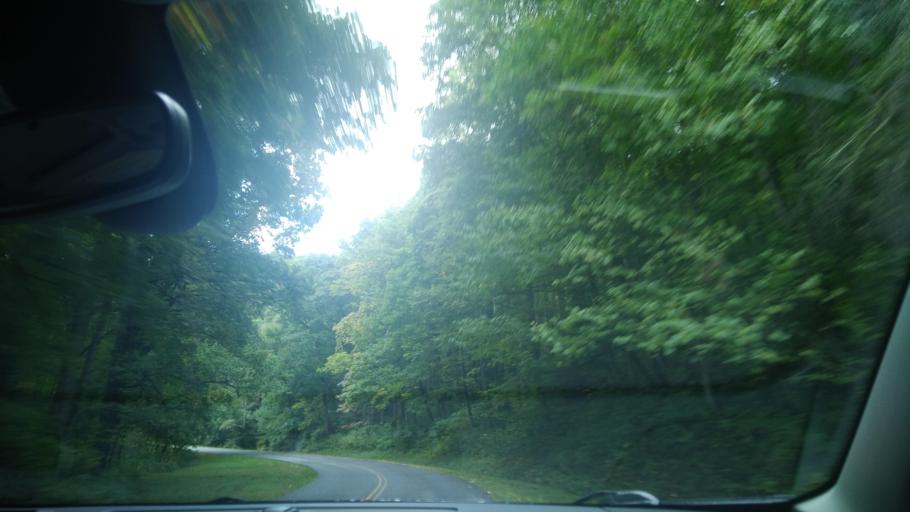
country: US
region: North Carolina
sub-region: Swain County
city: Cherokee
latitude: 35.5238
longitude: -83.2428
